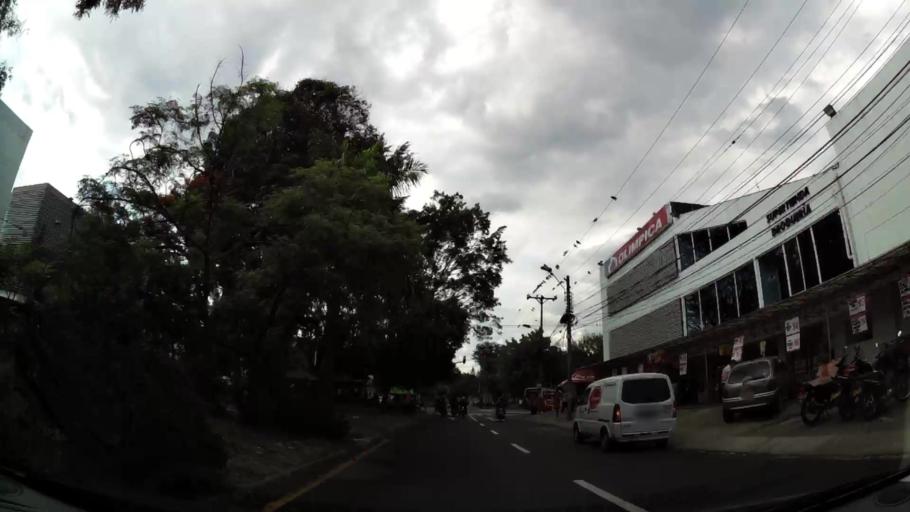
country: CO
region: Valle del Cauca
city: Cali
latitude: 3.4742
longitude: -76.4932
